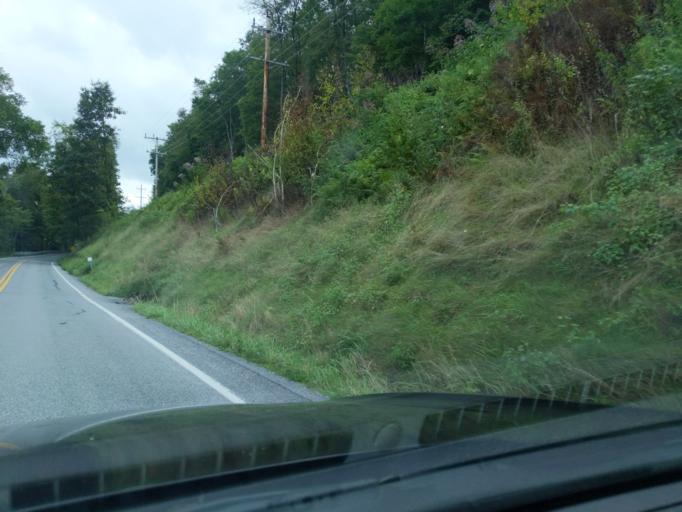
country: US
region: Pennsylvania
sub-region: Blair County
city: Duncansville
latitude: 40.3689
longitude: -78.5038
